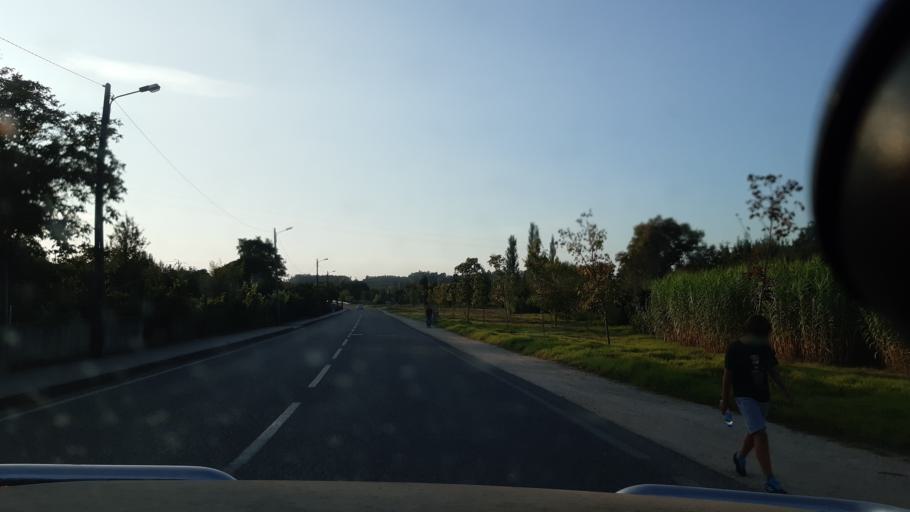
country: PT
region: Aveiro
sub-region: Agueda
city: Agueda
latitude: 40.5645
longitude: -8.4445
